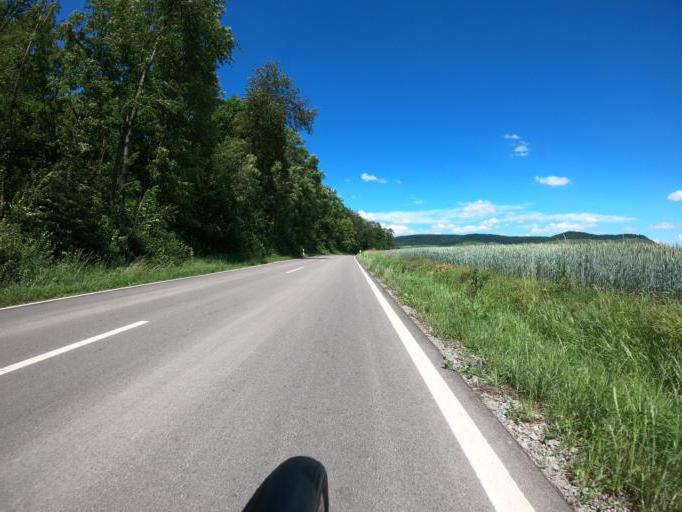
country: DE
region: Baden-Wuerttemberg
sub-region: Regierungsbezirk Stuttgart
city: Sersheim
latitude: 48.9848
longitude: 9.0210
